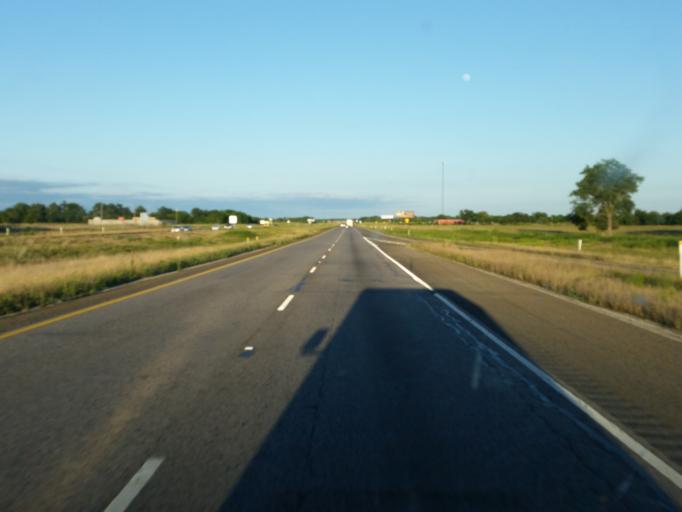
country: US
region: Texas
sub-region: Van Zandt County
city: Wills Point
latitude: 32.6546
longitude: -96.0918
